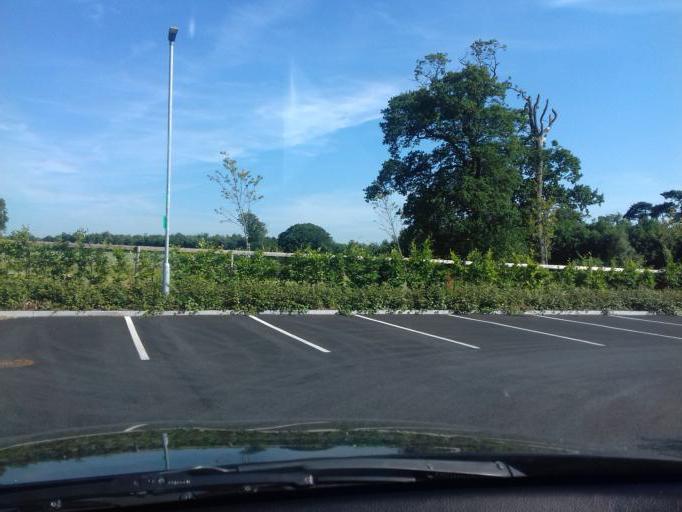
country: IE
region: Leinster
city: Castleknock
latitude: 53.3927
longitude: -6.3534
